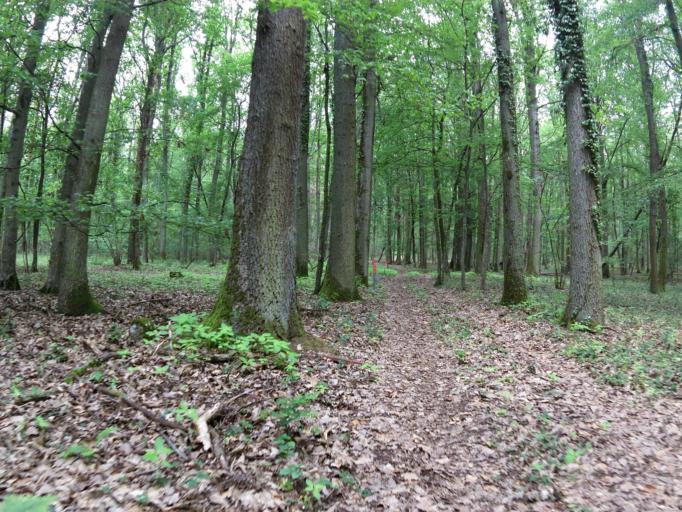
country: DE
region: Bavaria
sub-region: Regierungsbezirk Unterfranken
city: Sommerhausen
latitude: 49.7137
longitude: 10.0304
